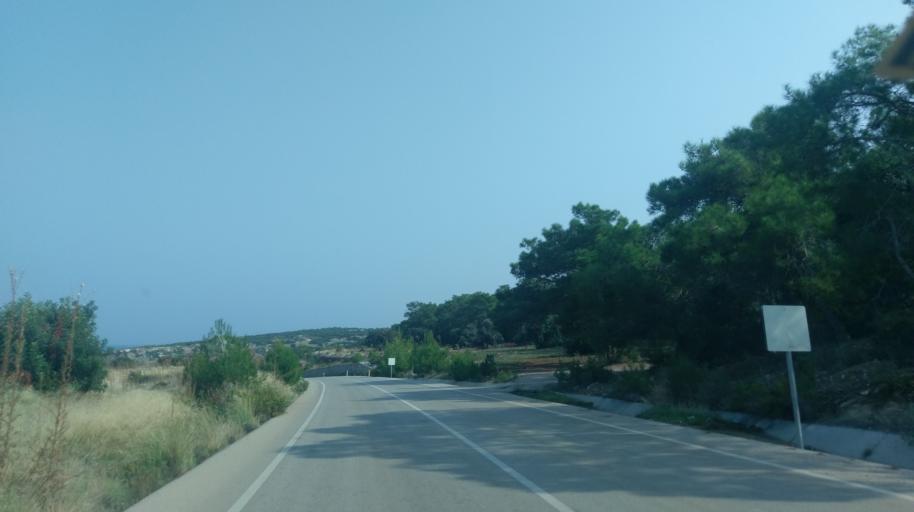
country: CY
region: Ammochostos
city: Trikomo
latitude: 35.4162
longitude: 33.8747
